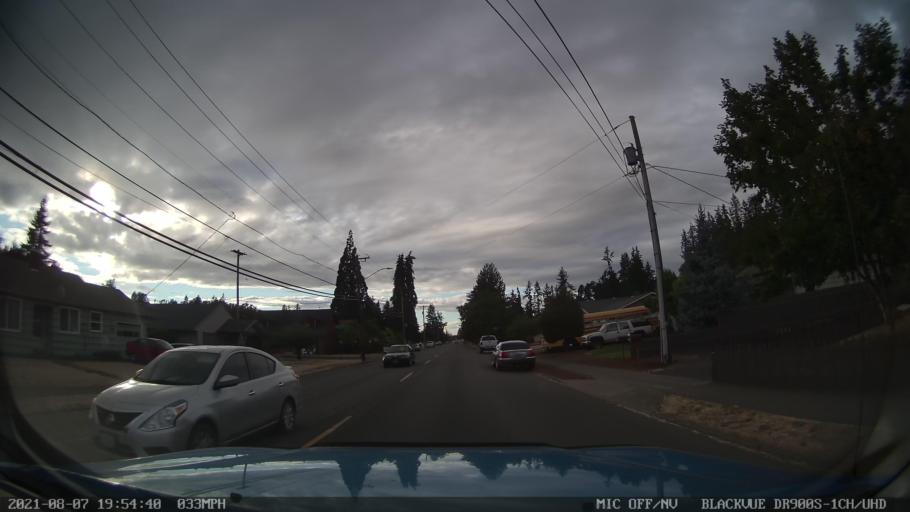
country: US
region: Oregon
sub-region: Marion County
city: Silverton
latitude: 44.9964
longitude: -122.7748
